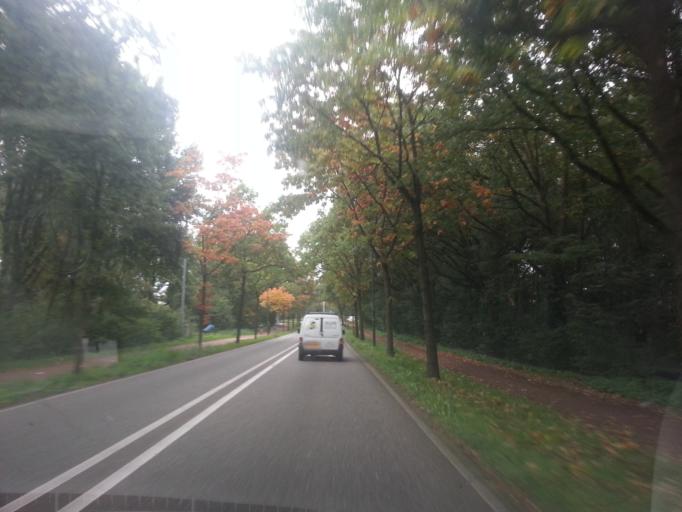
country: NL
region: North Brabant
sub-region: Gemeente Nuenen, Gerwen en Nederwetten
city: Nuenen
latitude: 51.4586
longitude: 5.5428
